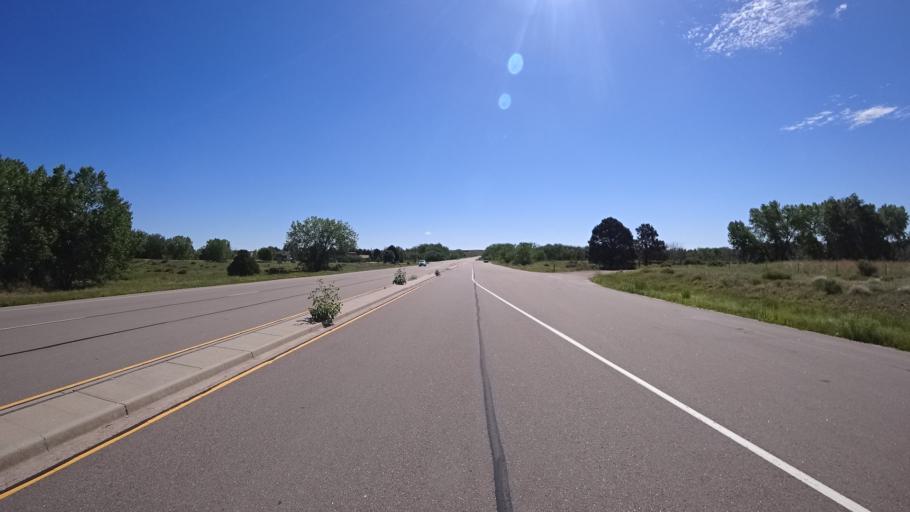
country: US
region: Colorado
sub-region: El Paso County
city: Security-Widefield
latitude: 38.7621
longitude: -104.6578
